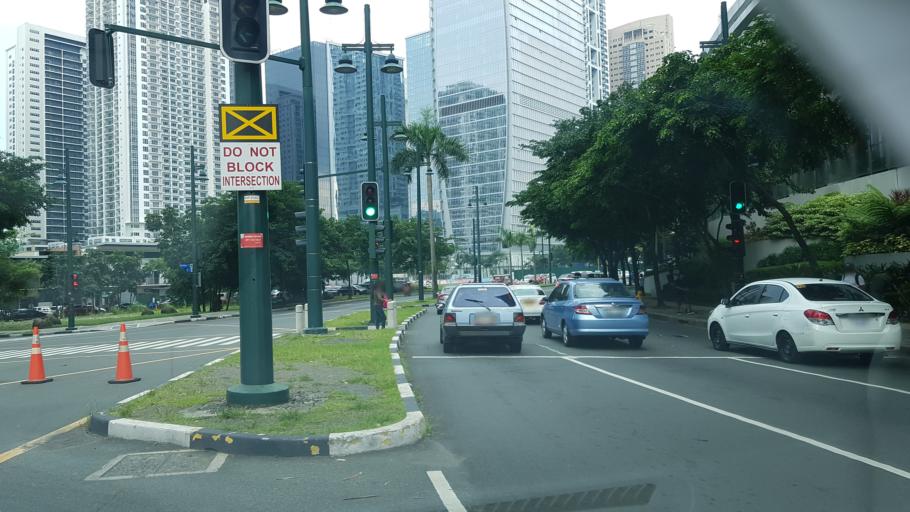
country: PH
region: Metro Manila
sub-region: Makati City
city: Makati City
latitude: 14.5465
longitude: 121.0477
